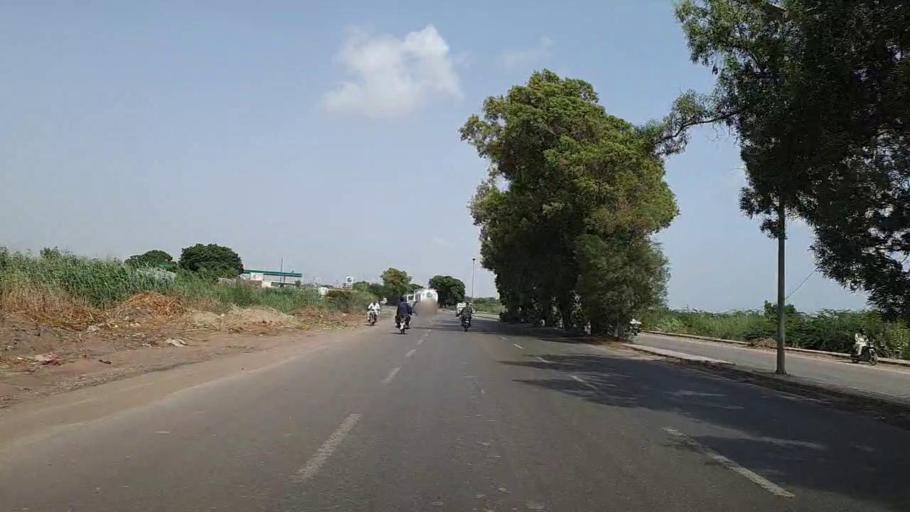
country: PK
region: Sindh
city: Malir Cantonment
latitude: 24.8634
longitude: 67.3157
